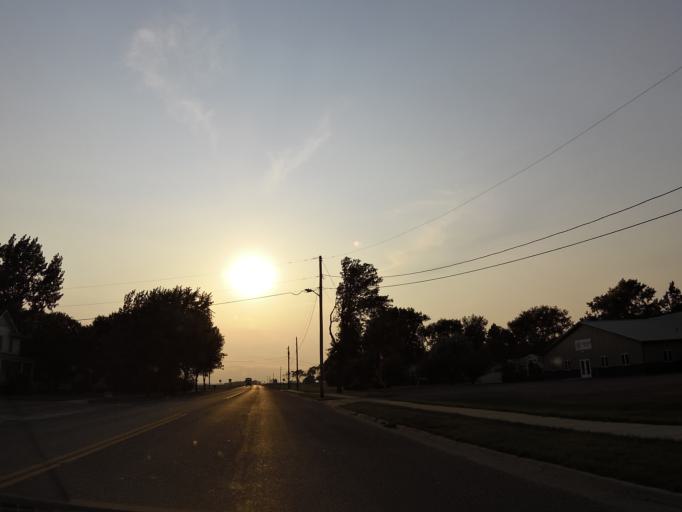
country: US
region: North Dakota
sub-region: Traill County
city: Mayville
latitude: 47.4985
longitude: -97.3769
